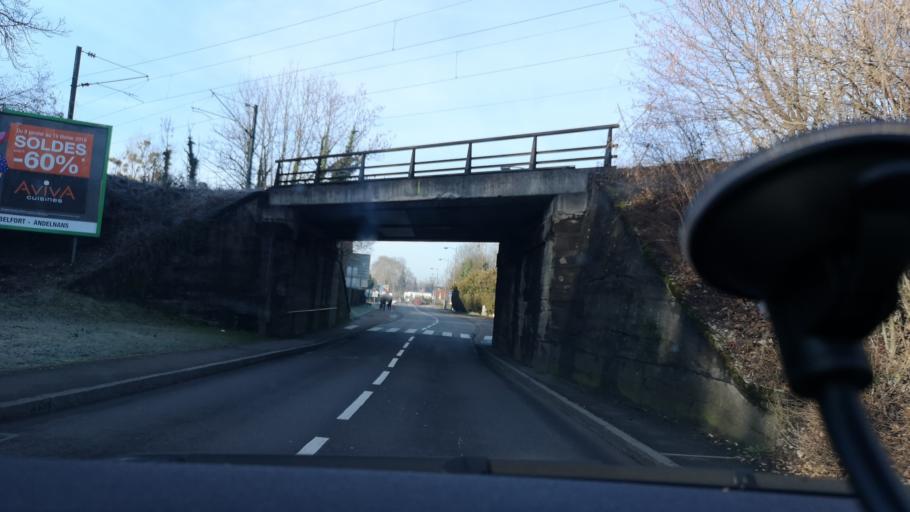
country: FR
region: Franche-Comte
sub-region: Departement du Doubs
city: Voujeaucourt
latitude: 47.4747
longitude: 6.7632
